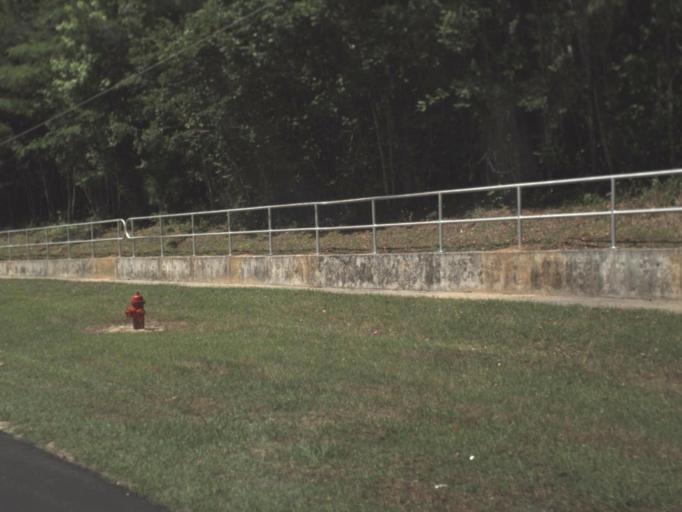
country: US
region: Florida
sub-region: Jackson County
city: Marianna
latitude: 30.7887
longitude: -85.2254
